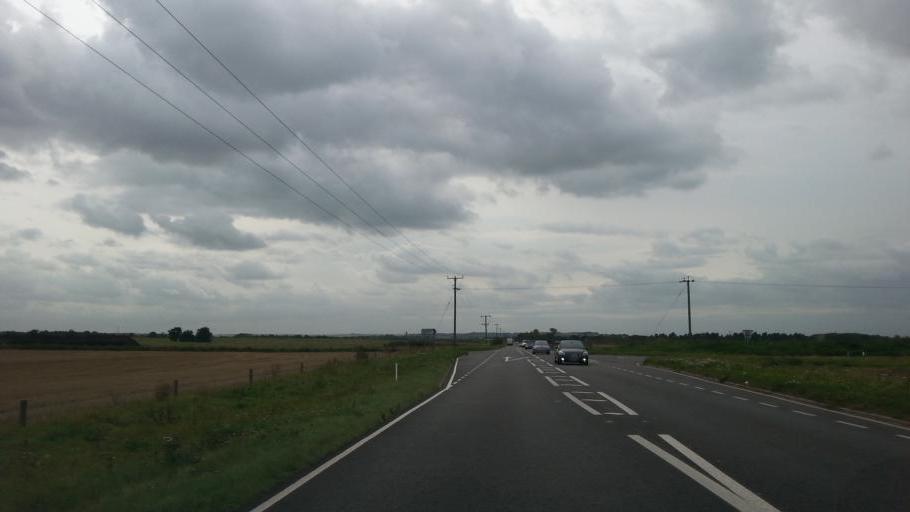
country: GB
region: England
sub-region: Cambridgeshire
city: Harston
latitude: 52.0771
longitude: 0.0880
